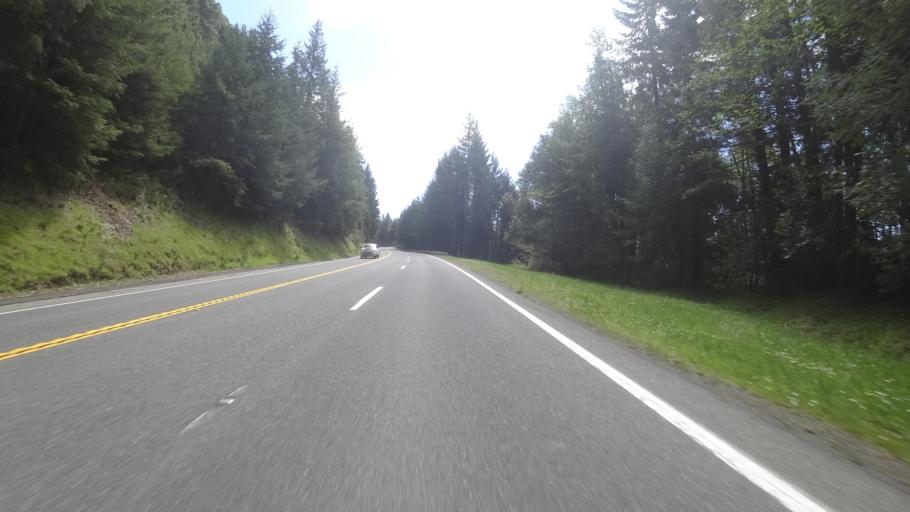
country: US
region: California
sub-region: Humboldt County
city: Blue Lake
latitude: 40.9337
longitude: -123.8642
